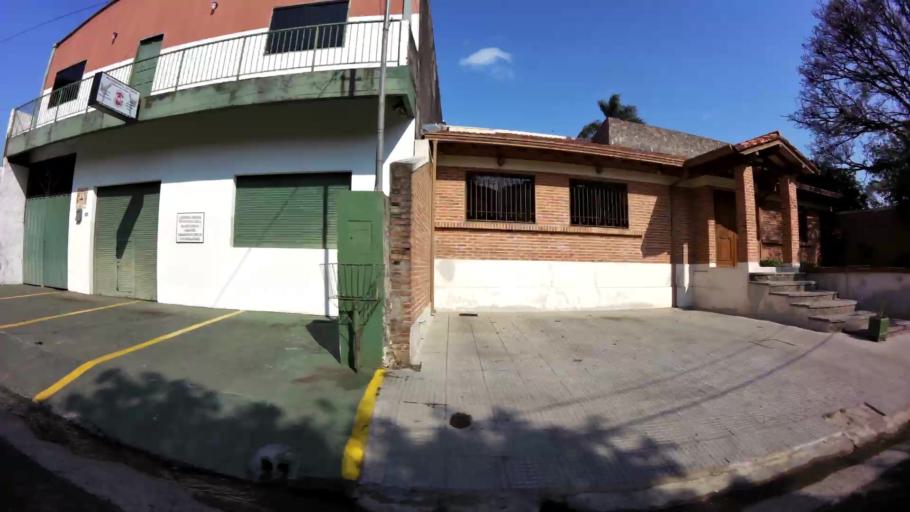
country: PY
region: Asuncion
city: Asuncion
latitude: -25.3080
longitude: -57.6229
